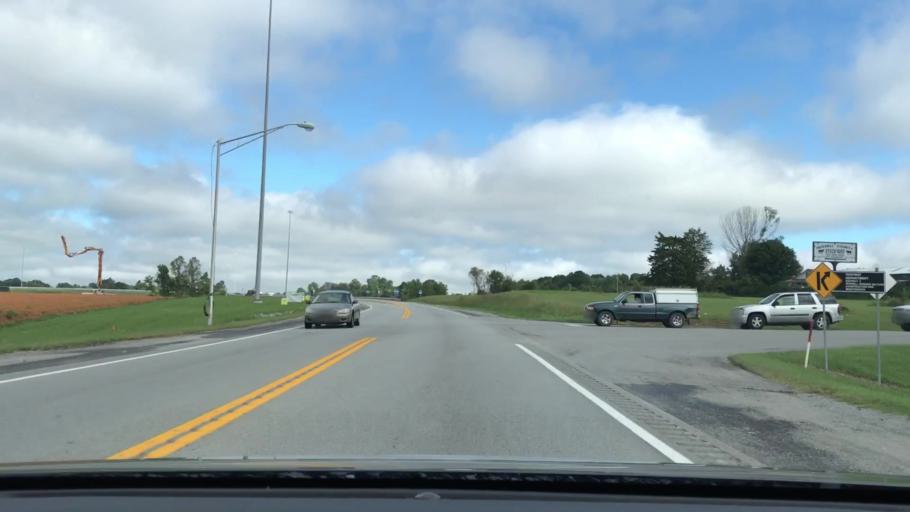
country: US
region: Kentucky
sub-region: Russell County
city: Russell Springs
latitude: 37.0459
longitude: -85.0705
